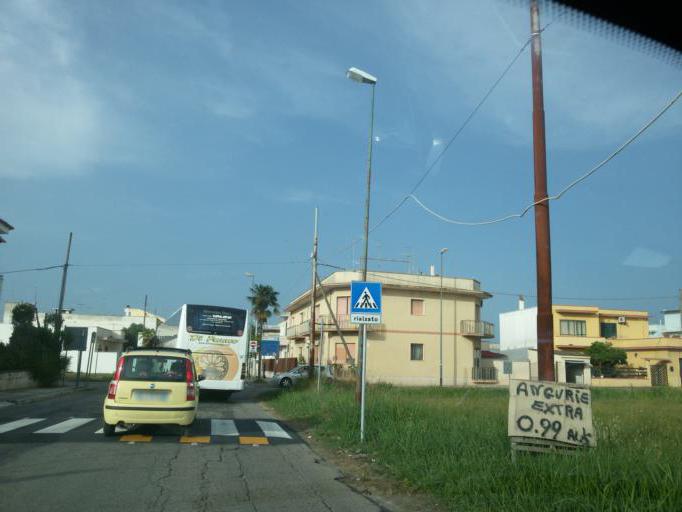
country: IT
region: Apulia
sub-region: Provincia di Brindisi
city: Cellino San Marco
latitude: 40.4685
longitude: 17.9599
